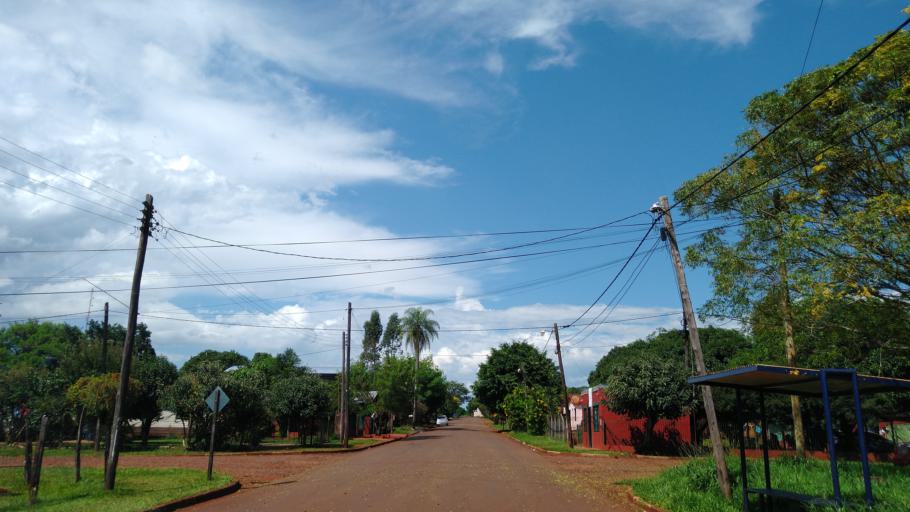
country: AR
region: Misiones
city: Puerto Libertad
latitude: -25.9689
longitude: -54.5747
